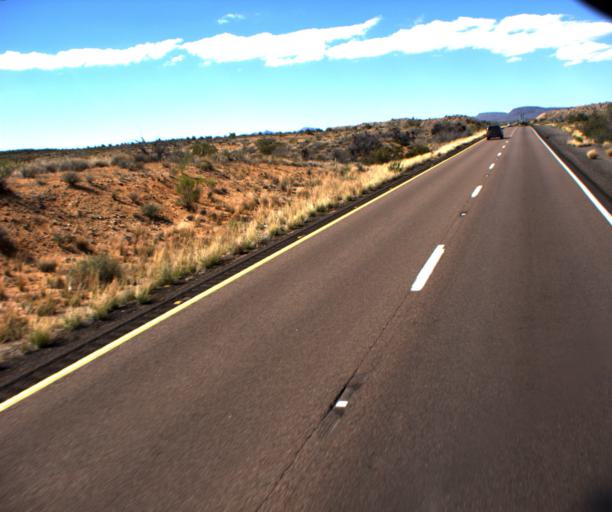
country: US
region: Arizona
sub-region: Mohave County
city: Kingman
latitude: 35.0695
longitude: -113.6651
